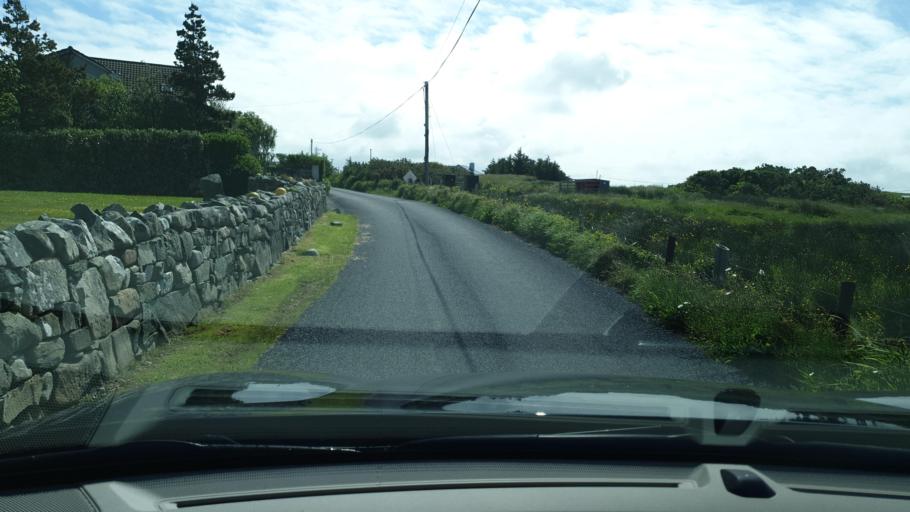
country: IE
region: Connaught
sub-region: County Galway
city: Clifden
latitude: 53.4364
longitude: -10.0760
